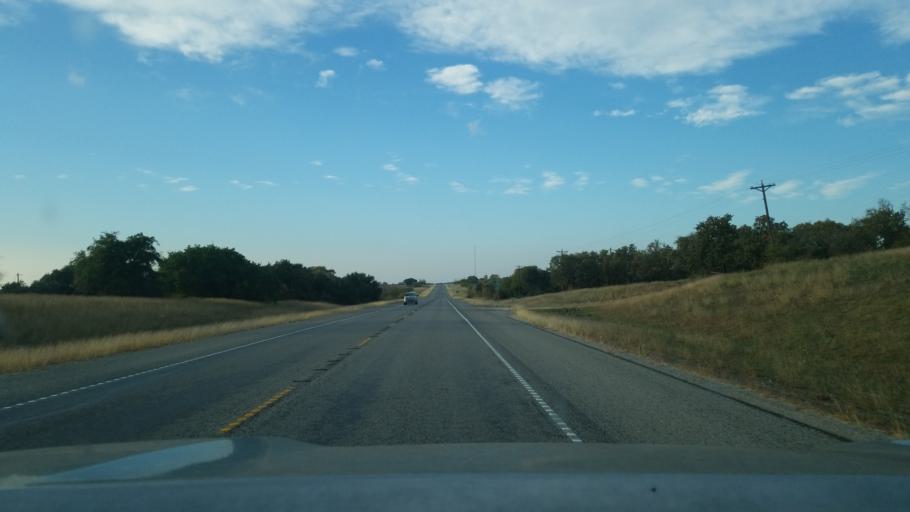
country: US
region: Texas
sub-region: Brown County
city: Lake Brownwood
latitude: 32.0224
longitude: -98.9280
